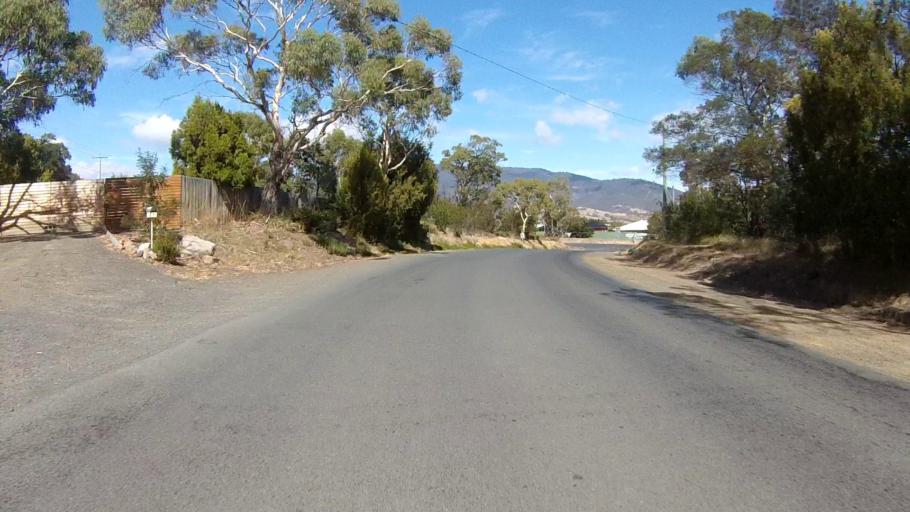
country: AU
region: Tasmania
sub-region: Brighton
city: Old Beach
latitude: -42.7698
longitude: 147.2708
